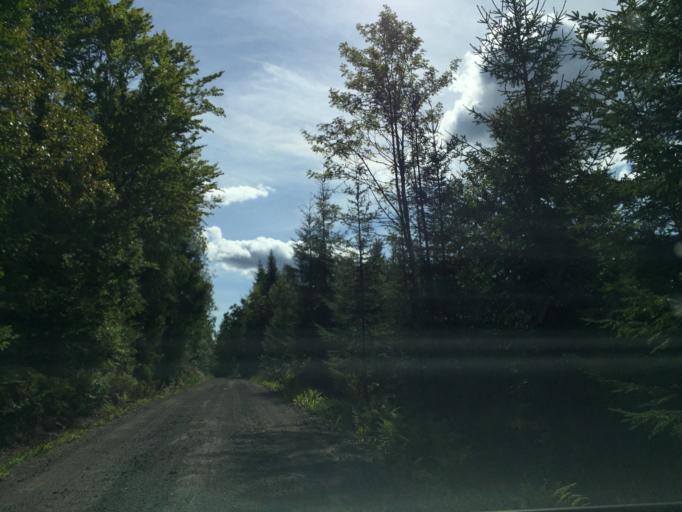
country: NO
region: Vestfold
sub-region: Hof
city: Hof
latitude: 59.4435
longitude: 10.1579
